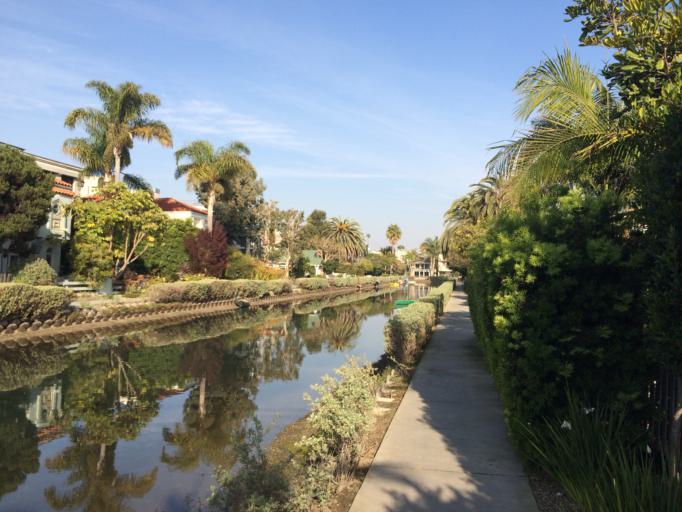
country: US
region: California
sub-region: Los Angeles County
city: Marina del Rey
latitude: 33.9839
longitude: -118.4659
